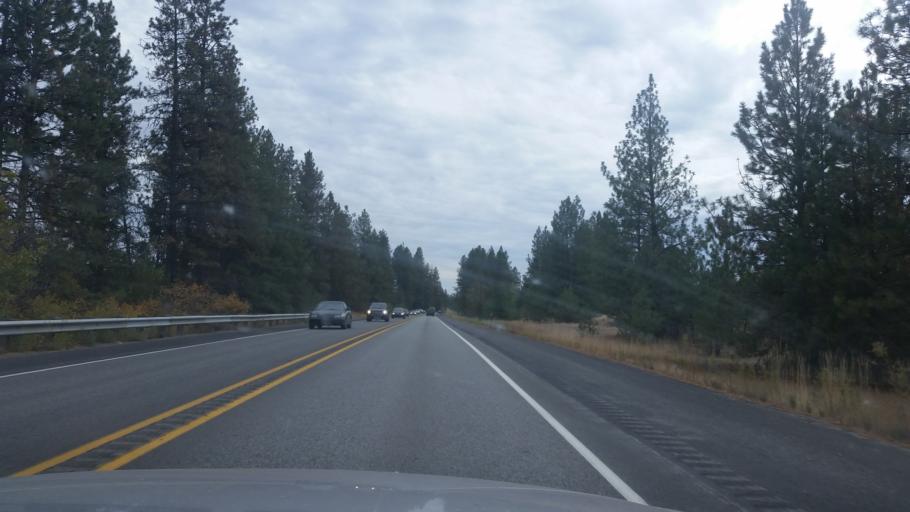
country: US
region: Washington
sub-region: Spokane County
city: Cheney
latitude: 47.5210
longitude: -117.5654
